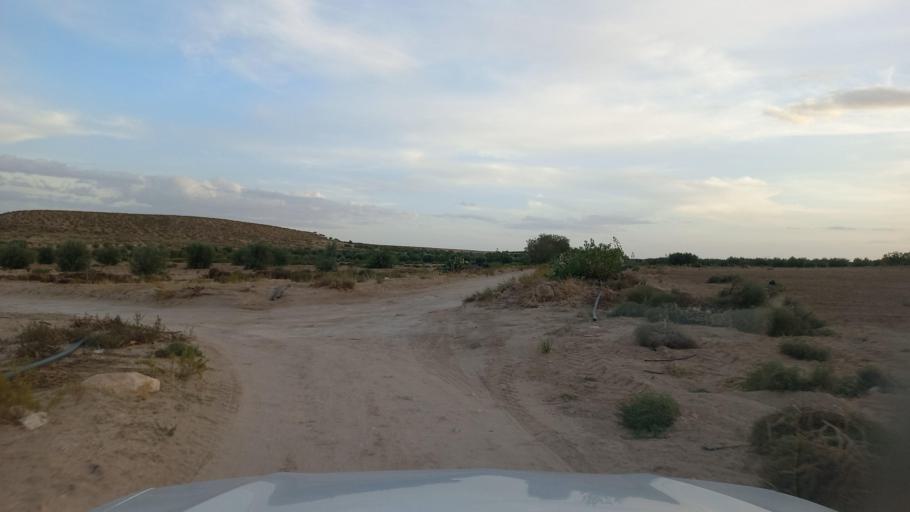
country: TN
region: Al Qasrayn
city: Sbiba
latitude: 35.4064
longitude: 9.0889
